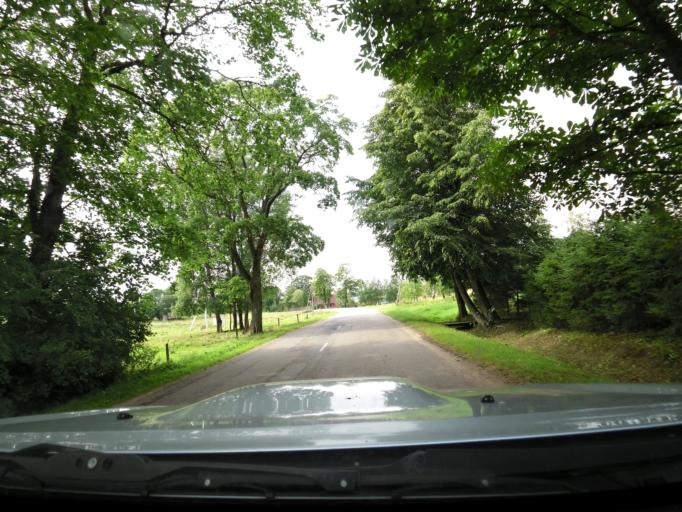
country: LT
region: Vilnius County
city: Elektrenai
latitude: 54.9027
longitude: 24.7244
